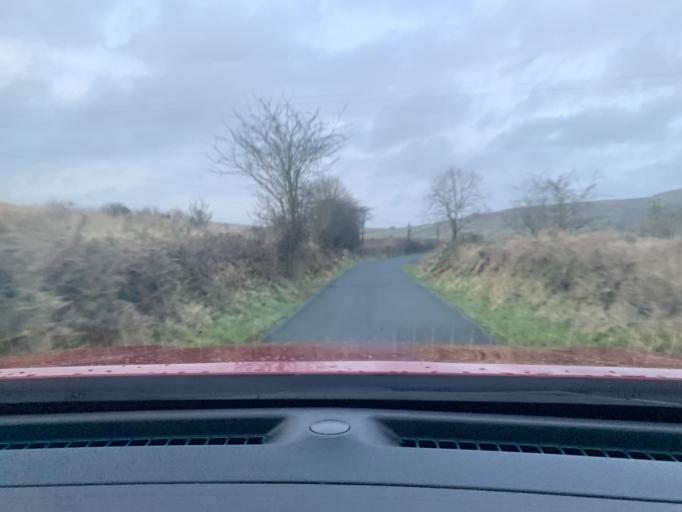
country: IE
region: Connaught
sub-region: Sligo
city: Ballymote
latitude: 54.0315
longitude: -8.4119
